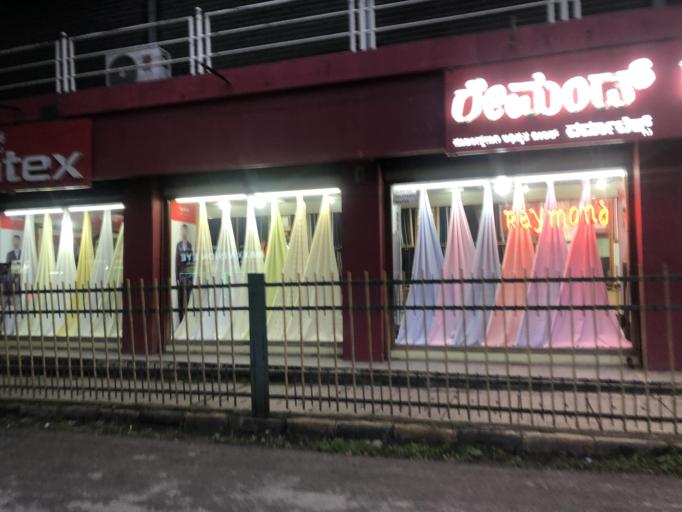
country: IN
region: Karnataka
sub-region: Bangalore Urban
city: Bangalore
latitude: 12.9723
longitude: 77.6269
